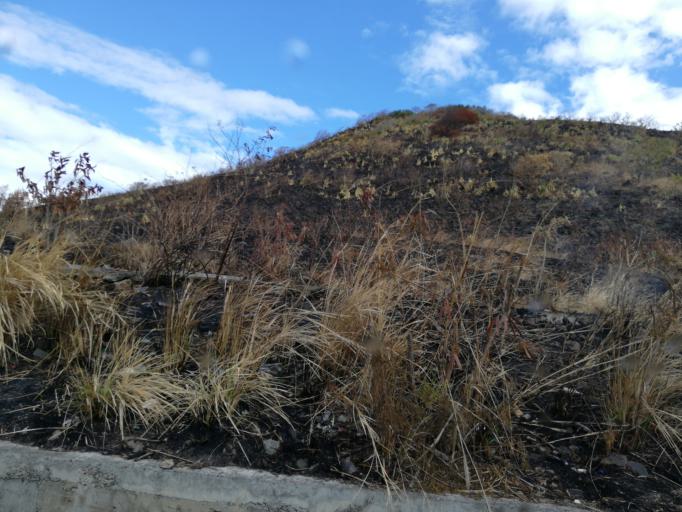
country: MU
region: Black River
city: Petite Riviere
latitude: -20.2044
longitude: 57.4637
